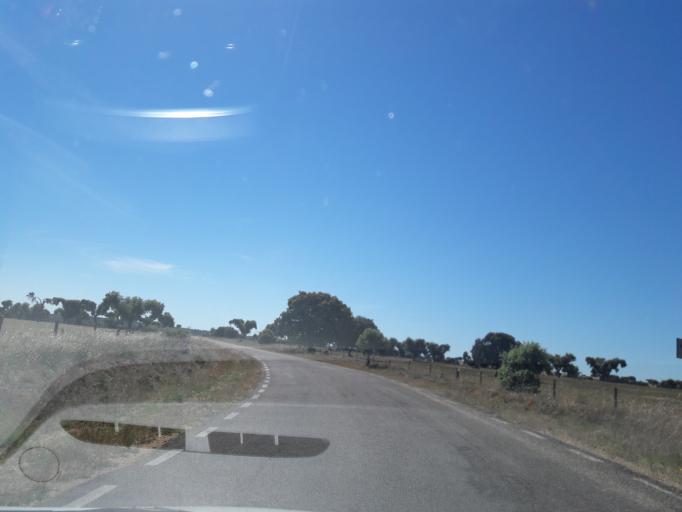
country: ES
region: Castille and Leon
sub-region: Provincia de Salamanca
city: Zarapicos
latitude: 41.0242
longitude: -5.8337
